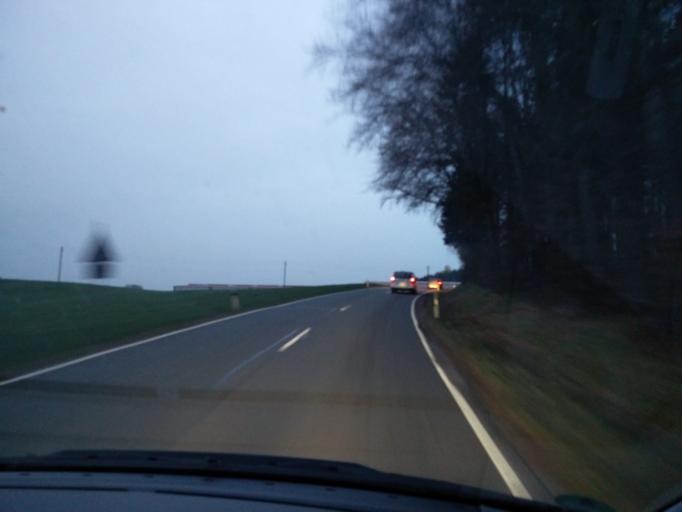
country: DE
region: Bavaria
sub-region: Upper Bavaria
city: Albaching
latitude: 48.1076
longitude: 12.1198
